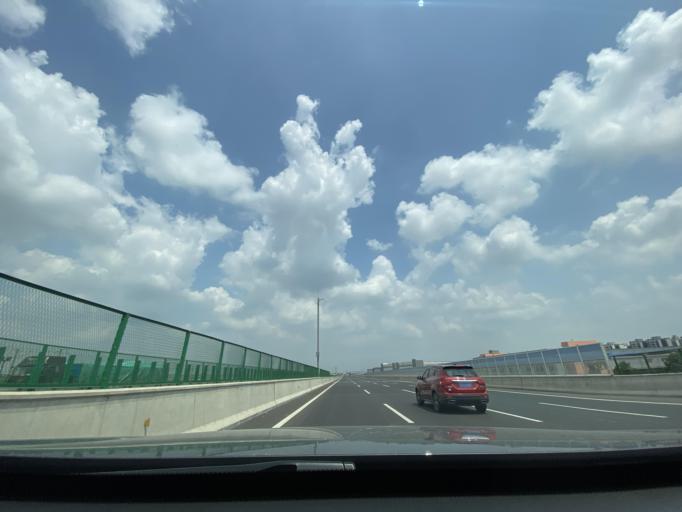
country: CN
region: Sichuan
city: Longquan
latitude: 30.5242
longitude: 104.1713
